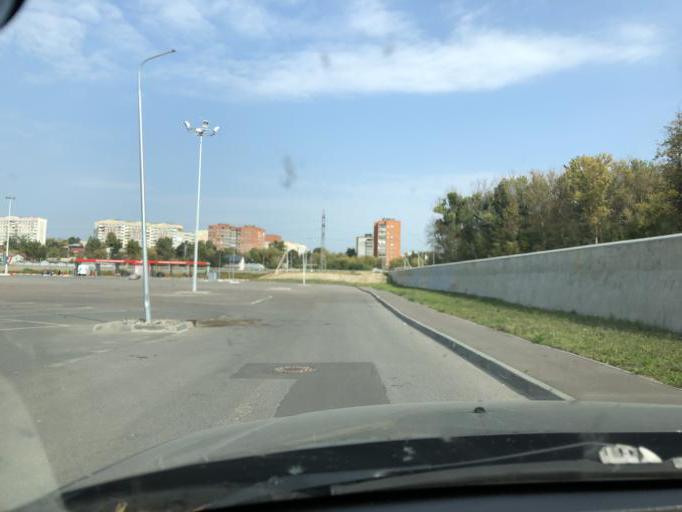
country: RU
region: Tula
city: Tula
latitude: 54.1919
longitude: 37.6427
